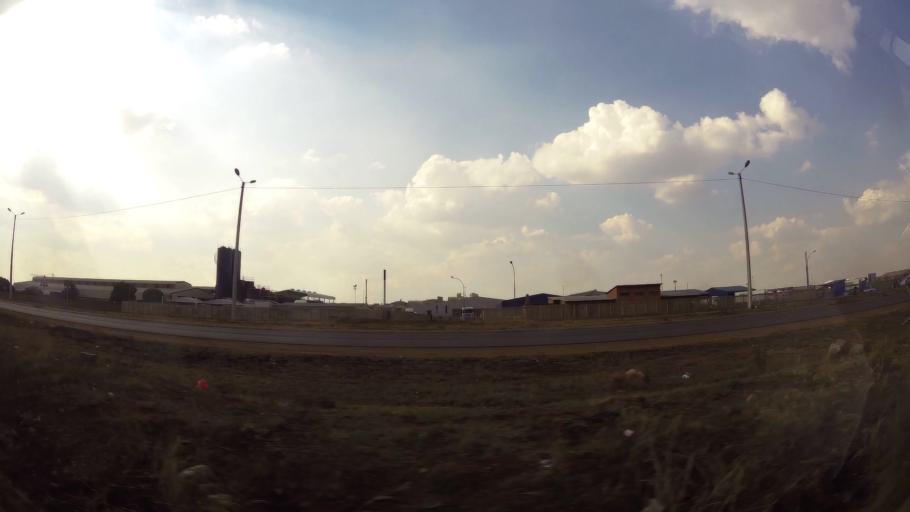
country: ZA
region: Gauteng
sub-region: Ekurhuleni Metropolitan Municipality
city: Germiston
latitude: -26.3061
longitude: 28.1942
